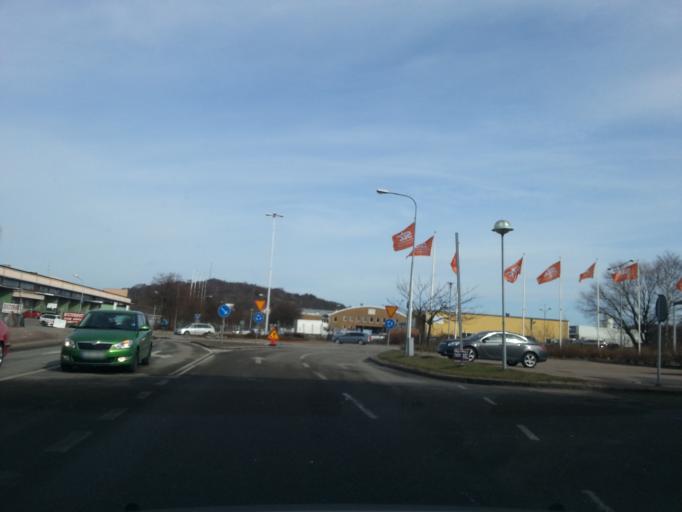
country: SE
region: Vaestra Goetaland
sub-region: Goteborg
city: Goeteborg
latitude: 57.7241
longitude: 11.9582
